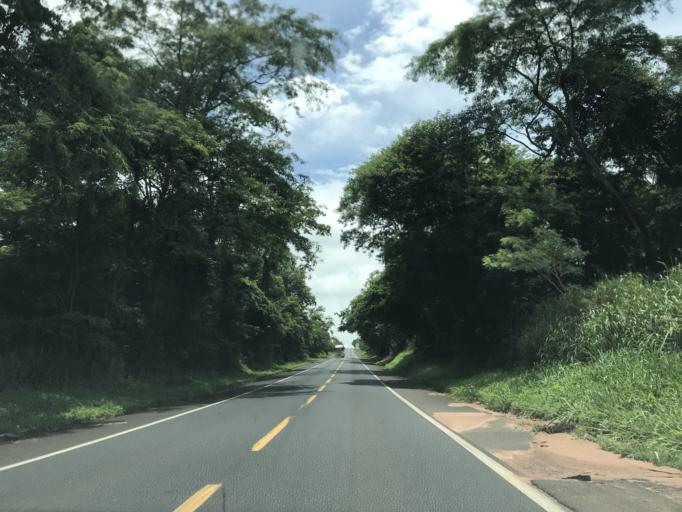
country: BR
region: Minas Gerais
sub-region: Prata
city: Prata
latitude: -19.6286
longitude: -48.9192
